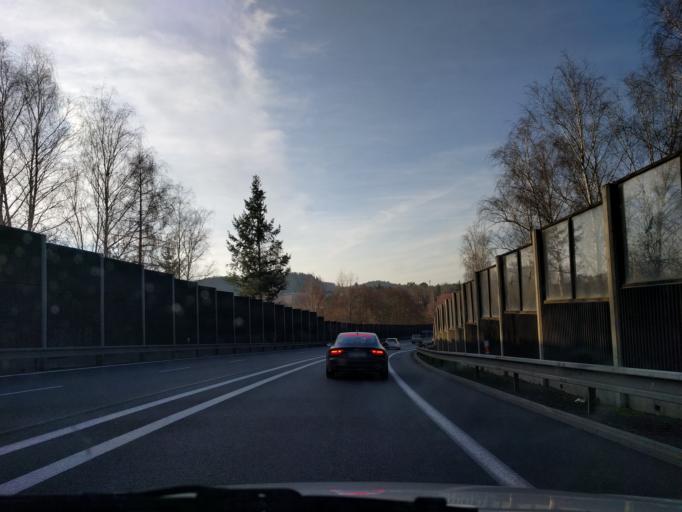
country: CZ
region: Central Bohemia
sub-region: Okres Praha-Vychod
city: Mnichovice
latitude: 49.9067
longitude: 14.7111
